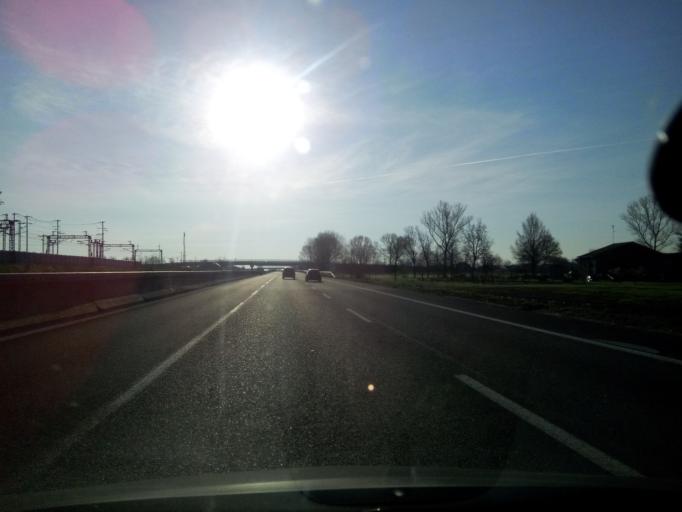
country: IT
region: Emilia-Romagna
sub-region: Provincia di Parma
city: Fontanellato
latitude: 44.8790
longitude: 10.1553
